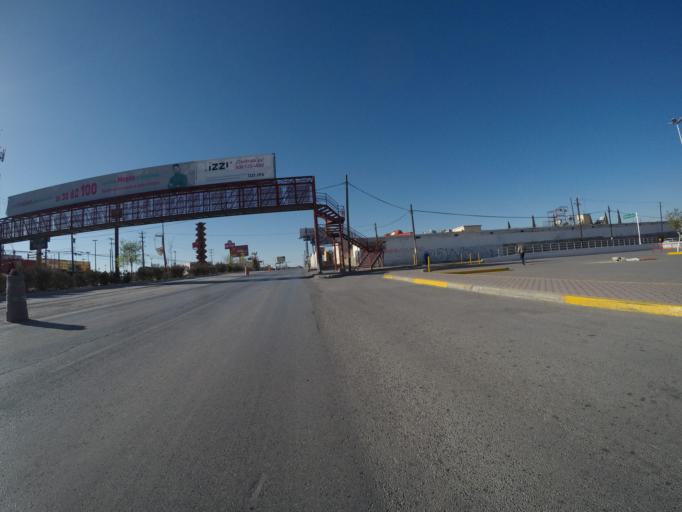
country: MX
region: Chihuahua
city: Ciudad Juarez
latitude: 31.6774
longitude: -106.4248
